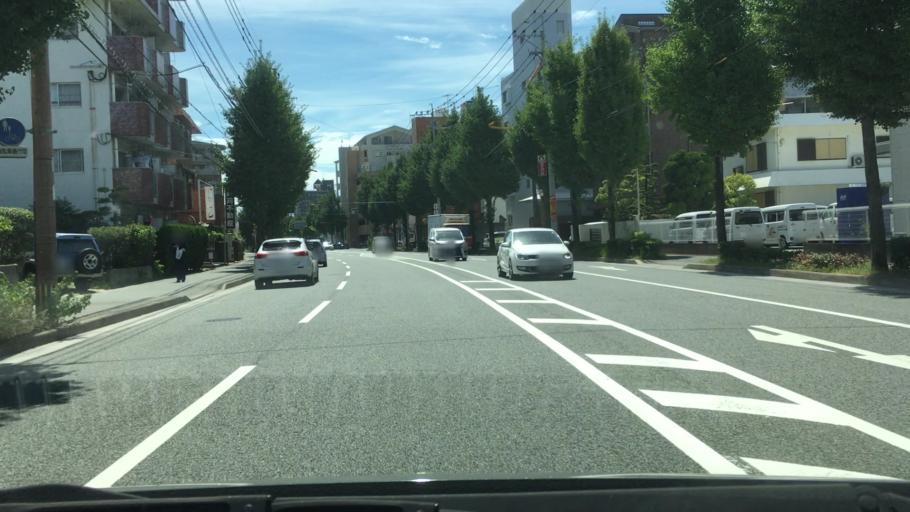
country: JP
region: Fukuoka
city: Fukuoka-shi
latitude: 33.5650
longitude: 130.4290
